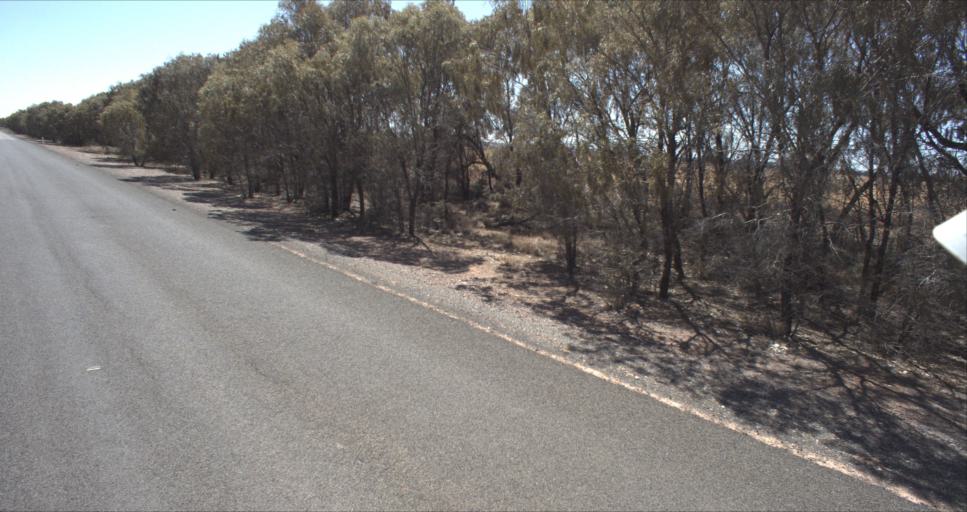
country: AU
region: New South Wales
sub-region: Leeton
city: Leeton
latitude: -34.4853
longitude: 146.2898
